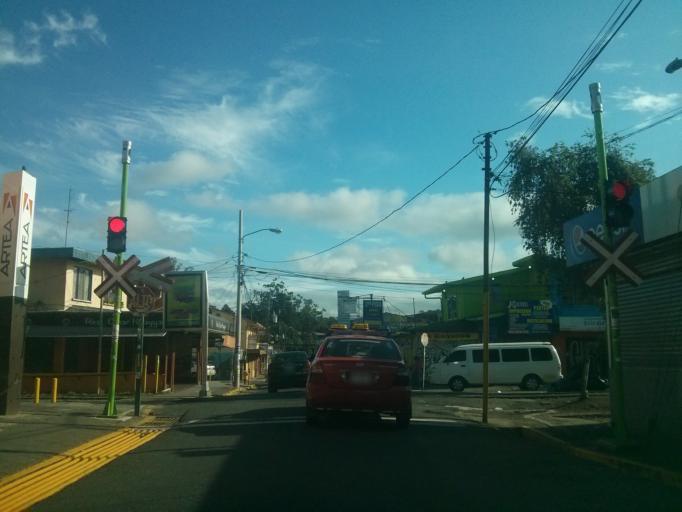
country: CR
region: San Jose
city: San Pedro
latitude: 9.9335
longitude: -84.0511
